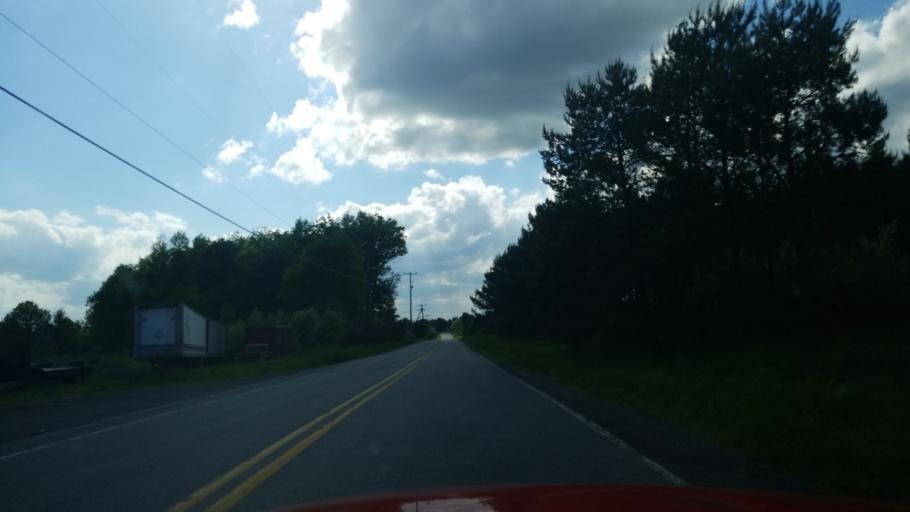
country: US
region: Pennsylvania
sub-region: Clearfield County
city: Hyde
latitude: 40.9745
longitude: -78.4450
